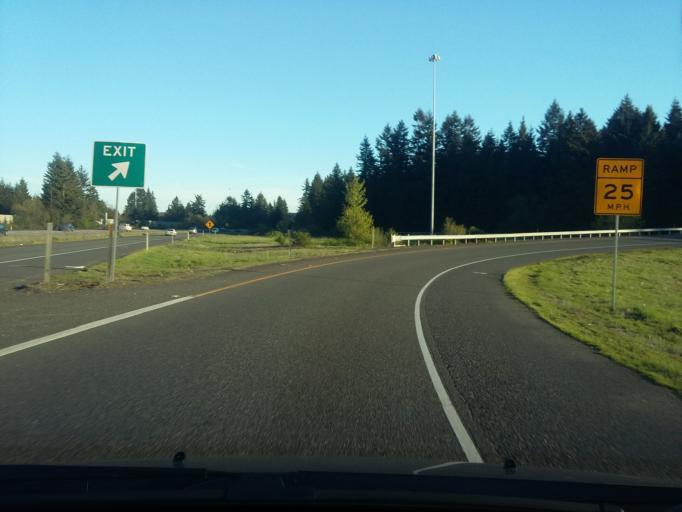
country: US
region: Washington
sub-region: Clark County
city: Orchards
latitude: 45.6559
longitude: -122.5706
